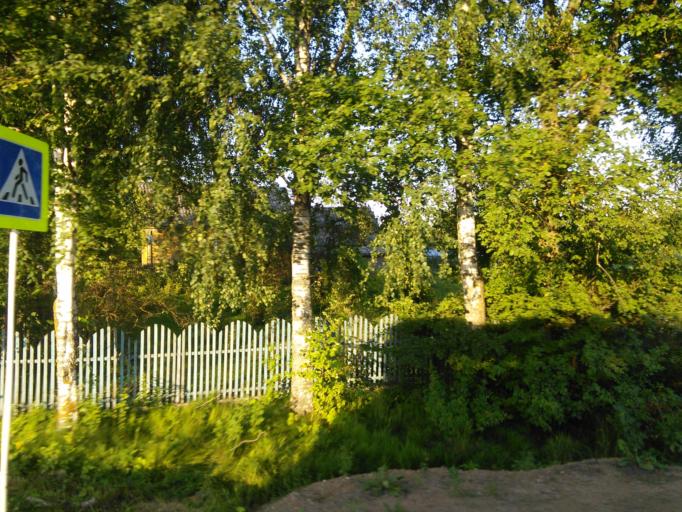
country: RU
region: Vologda
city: Chagoda
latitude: 59.1620
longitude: 35.3204
